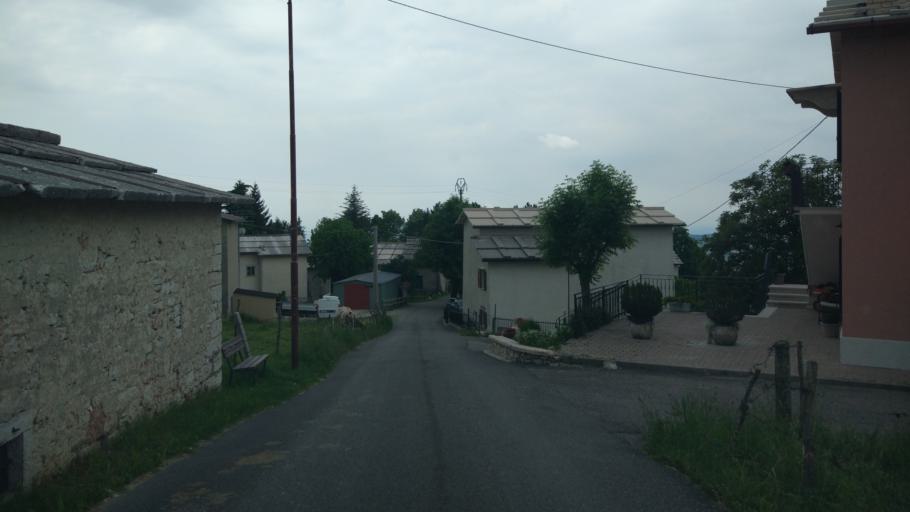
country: IT
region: Veneto
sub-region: Provincia di Verona
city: Erbezzo
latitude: 45.6465
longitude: 11.0002
